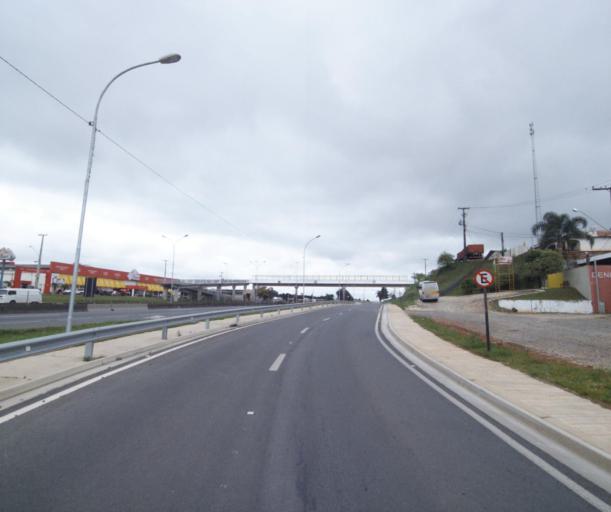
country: BR
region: Parana
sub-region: Quatro Barras
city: Quatro Barras
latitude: -25.3675
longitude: -49.1050
